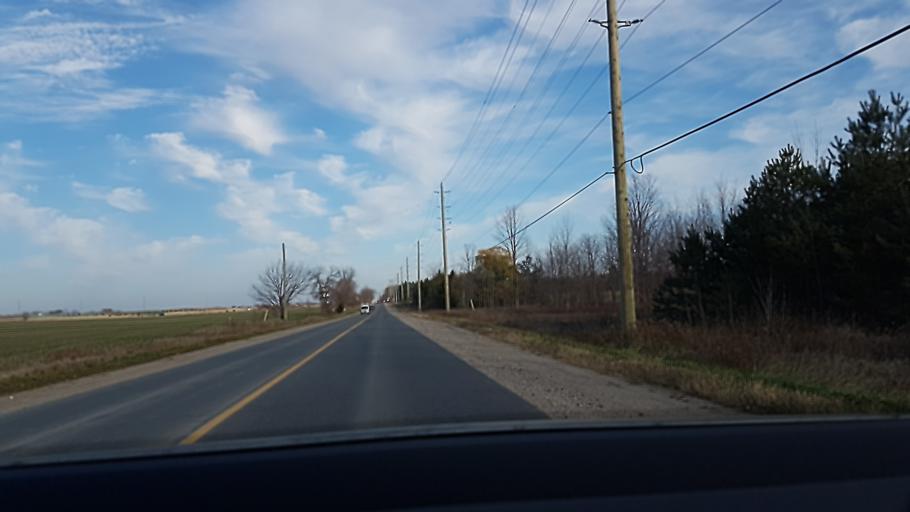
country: CA
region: Ontario
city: Barrie
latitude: 44.3762
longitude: -79.5620
